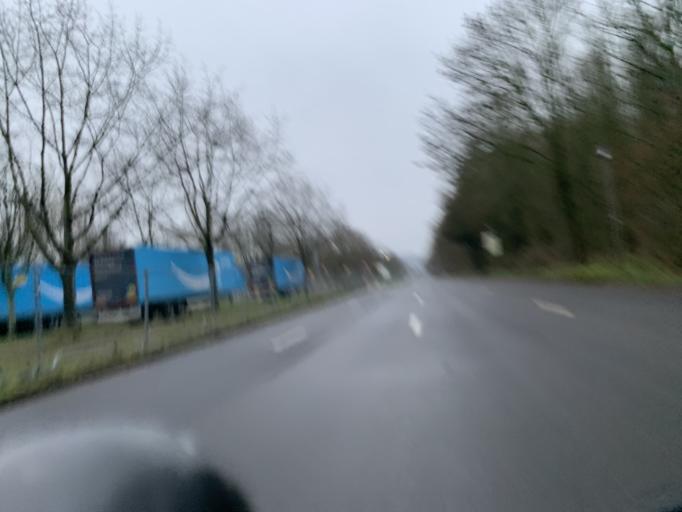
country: DE
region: North Rhine-Westphalia
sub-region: Regierungsbezirk Dusseldorf
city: Meerbusch
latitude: 51.2663
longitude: 6.7181
